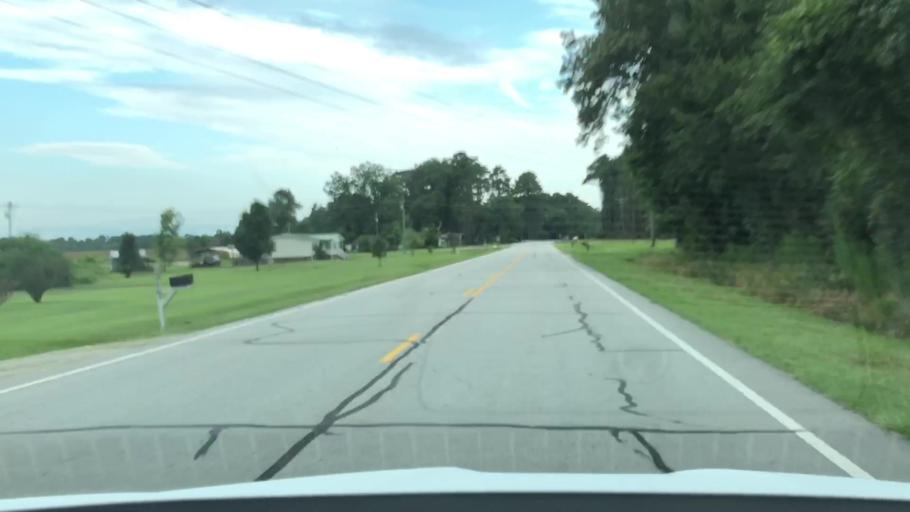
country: US
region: North Carolina
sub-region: Lenoir County
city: Kinston
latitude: 35.1190
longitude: -77.5151
